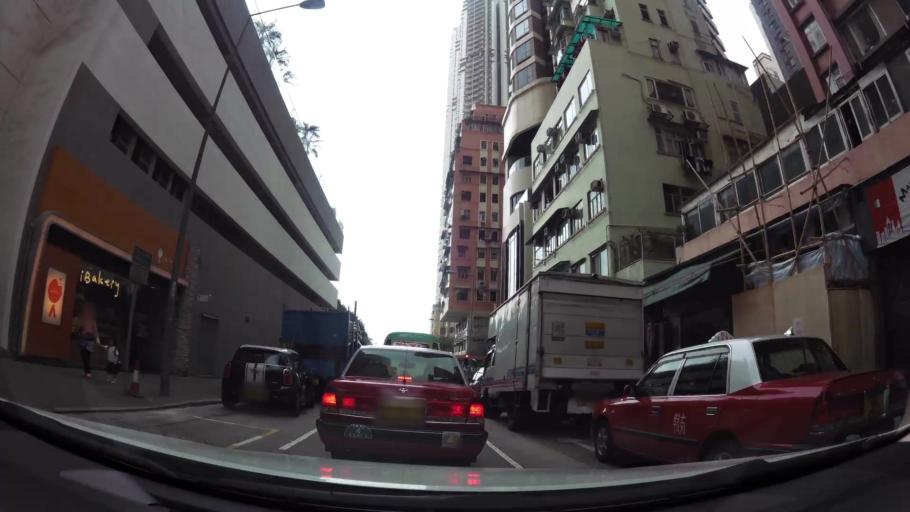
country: HK
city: Hong Kong
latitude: 22.2818
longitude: 114.1262
